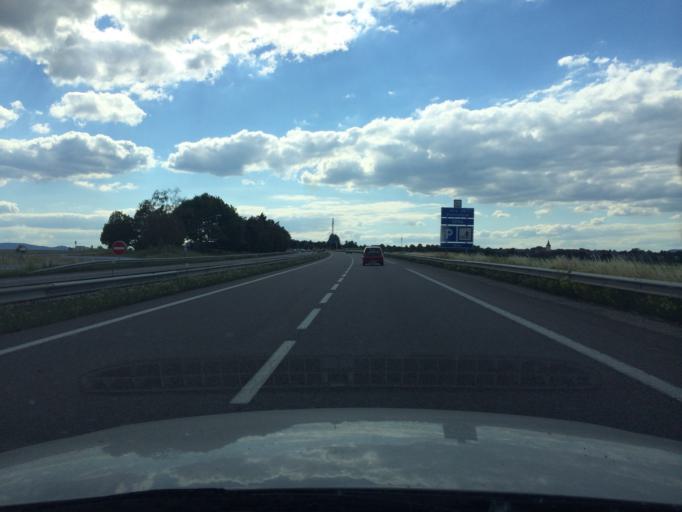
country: FR
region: Alsace
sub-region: Departement du Bas-Rhin
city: Dettwiller
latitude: 48.7709
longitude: 7.4974
